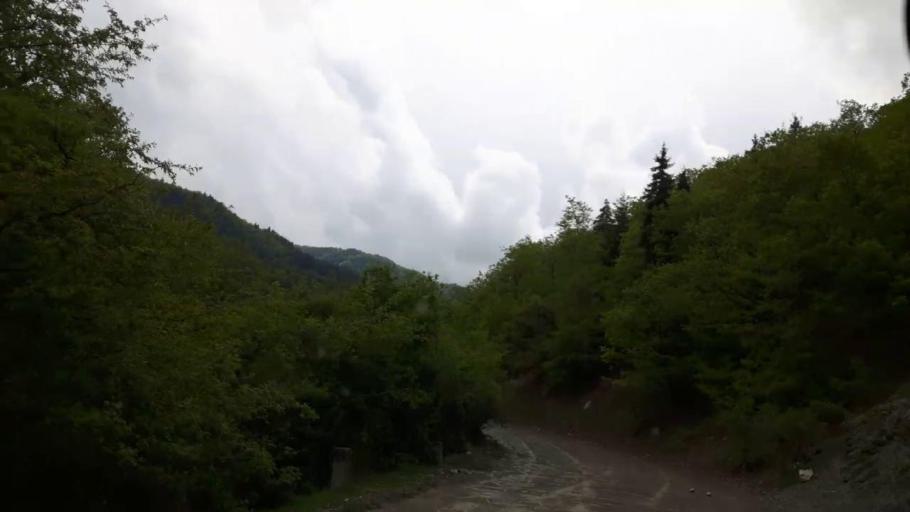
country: GE
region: Shida Kartli
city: Gori
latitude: 41.8768
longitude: 43.9896
